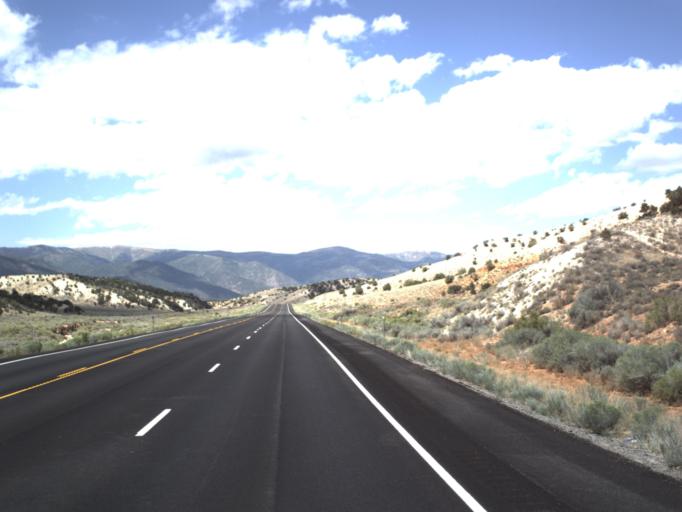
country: US
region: Utah
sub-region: Sevier County
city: Aurora
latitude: 38.9764
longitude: -111.9749
